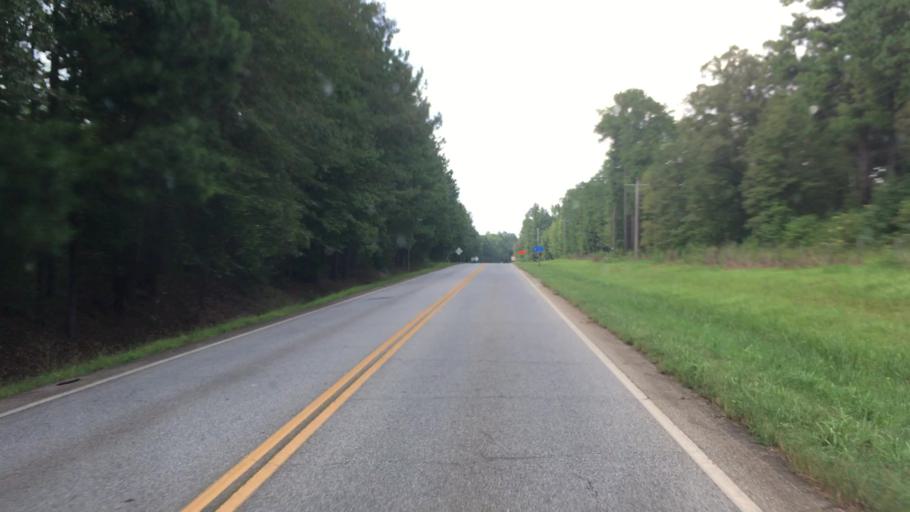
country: US
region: Georgia
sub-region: Monroe County
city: Forsyth
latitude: 33.1202
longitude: -83.8712
